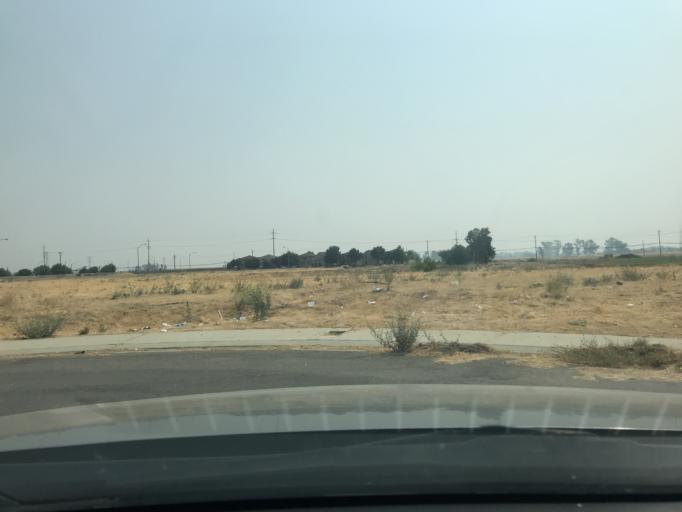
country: US
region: California
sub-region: Merced County
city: Merced
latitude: 37.3445
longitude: -120.4723
